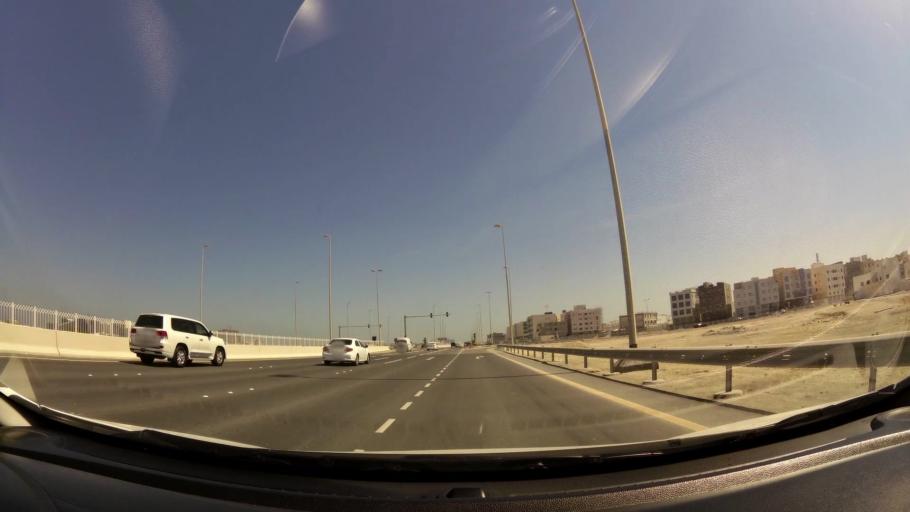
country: BH
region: Muharraq
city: Al Hadd
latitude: 26.2843
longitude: 50.6442
